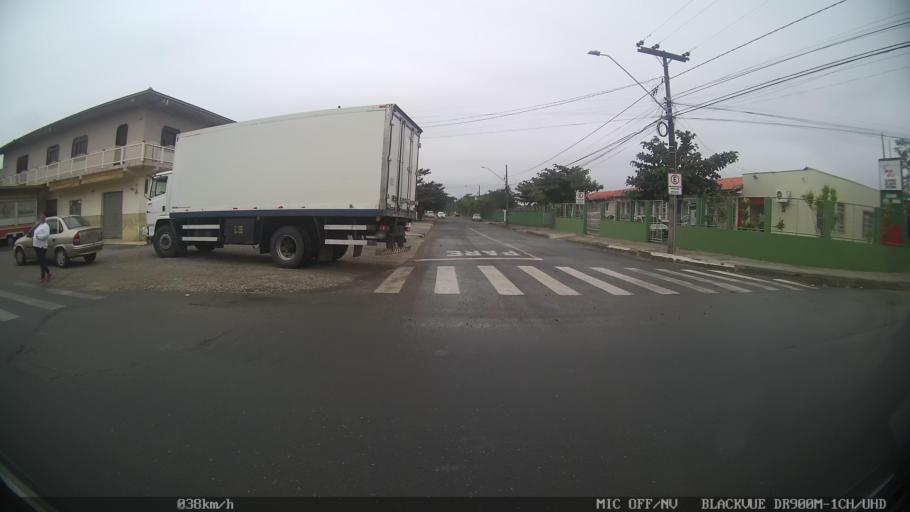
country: BR
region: Santa Catarina
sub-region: Joinville
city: Joinville
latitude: -26.2430
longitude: -48.8119
